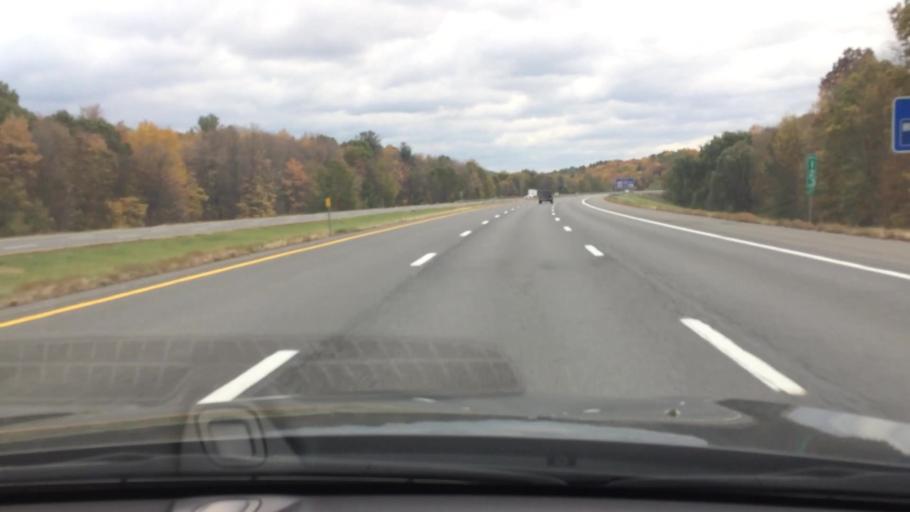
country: US
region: New York
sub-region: Rensselaer County
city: East Greenbush
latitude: 42.5917
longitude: -73.6775
